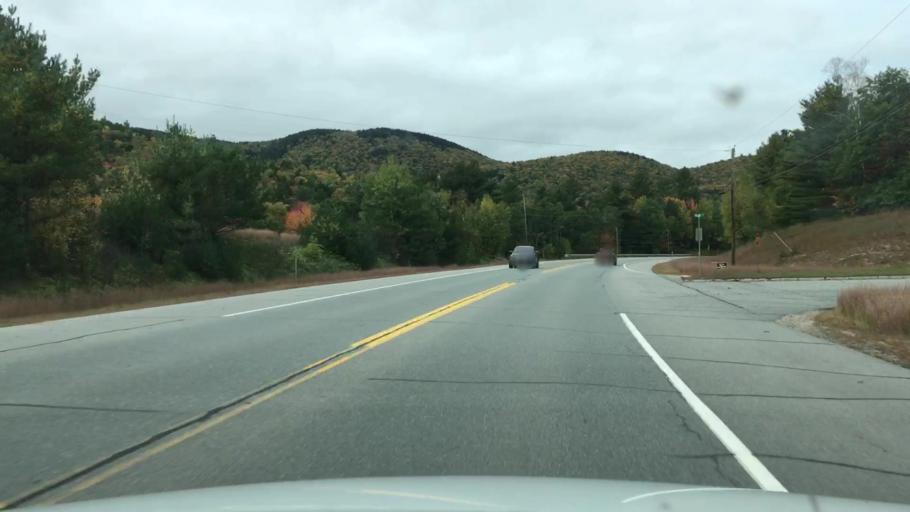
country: US
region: New Hampshire
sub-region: Coos County
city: Gorham
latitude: 44.3971
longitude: -71.0651
